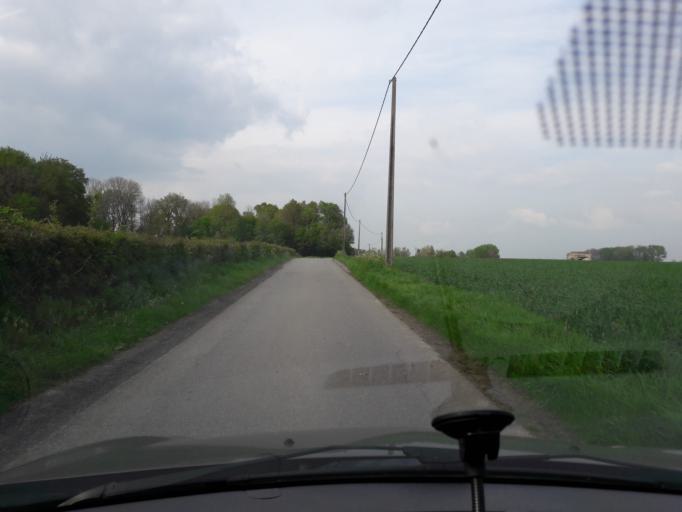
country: FR
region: Nord-Pas-de-Calais
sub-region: Departement du Nord
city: Marpent
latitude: 50.2436
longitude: 4.0789
